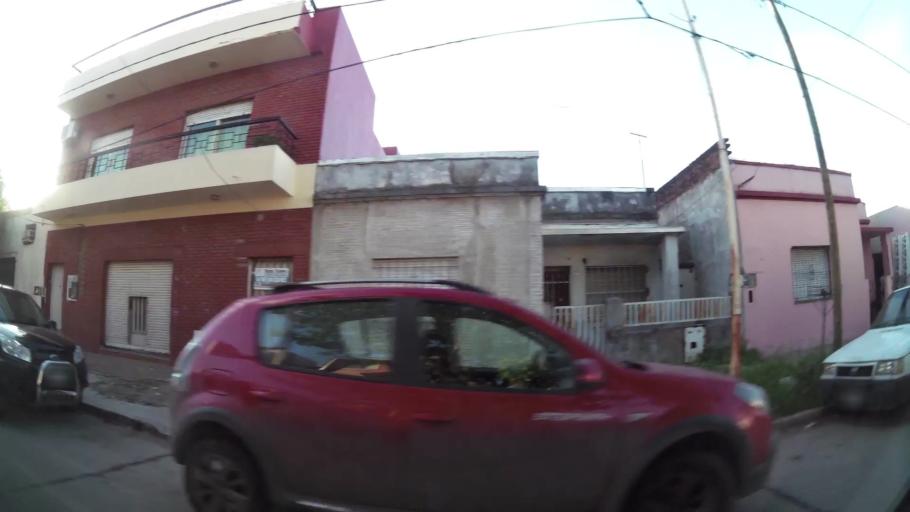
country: AR
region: Buenos Aires F.D.
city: Villa Lugano
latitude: -34.6914
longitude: -58.4860
